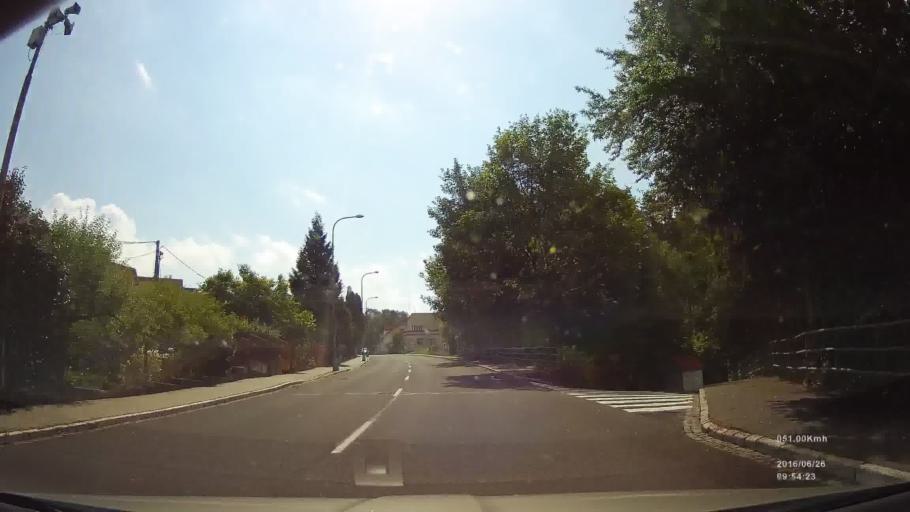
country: SK
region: Banskobystricky
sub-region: Okres Banska Bystrica
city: Zvolen
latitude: 48.6111
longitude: 19.1519
